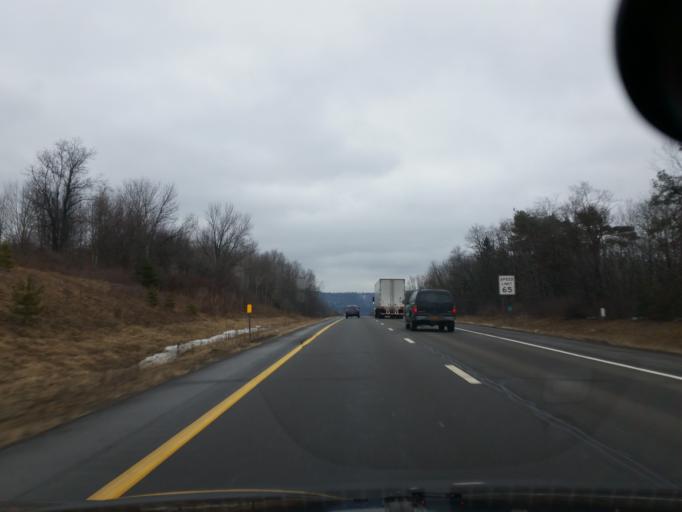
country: US
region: Pennsylvania
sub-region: Susquehanna County
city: Hallstead
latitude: 42.0356
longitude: -75.7895
